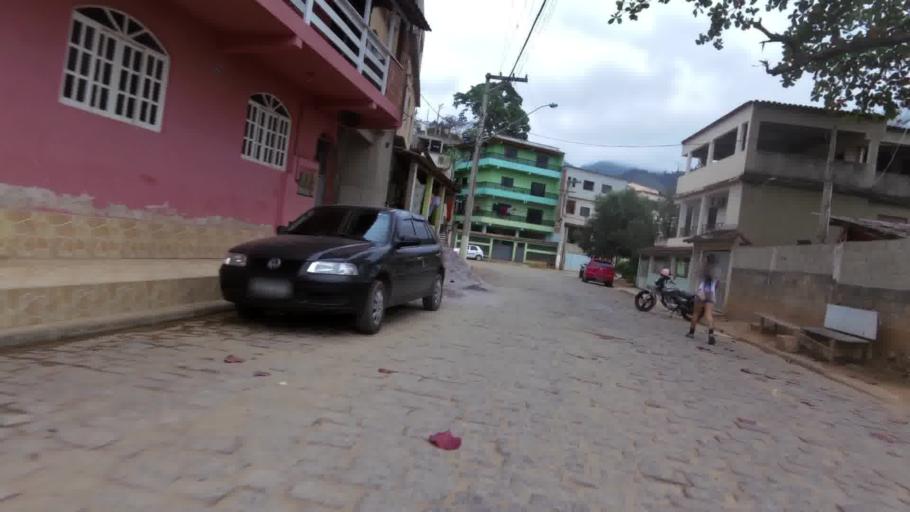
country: BR
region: Espirito Santo
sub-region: Alfredo Chaves
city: Alfredo Chaves
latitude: -20.6380
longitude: -40.7493
